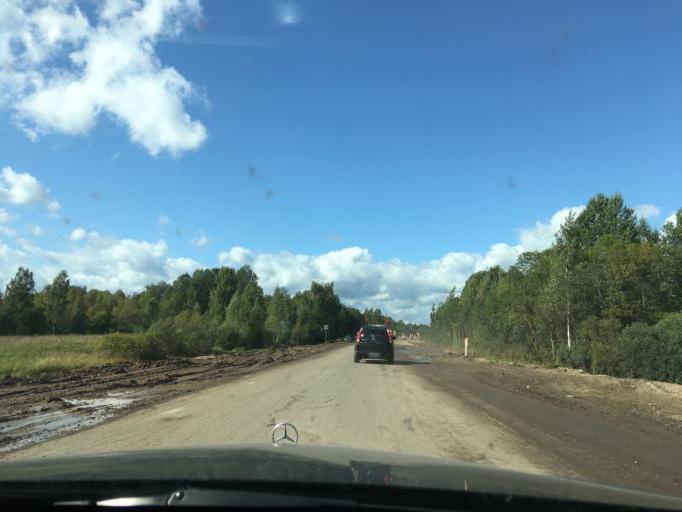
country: RU
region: Pskov
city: Velikiye Luki
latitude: 56.2719
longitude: 30.3521
